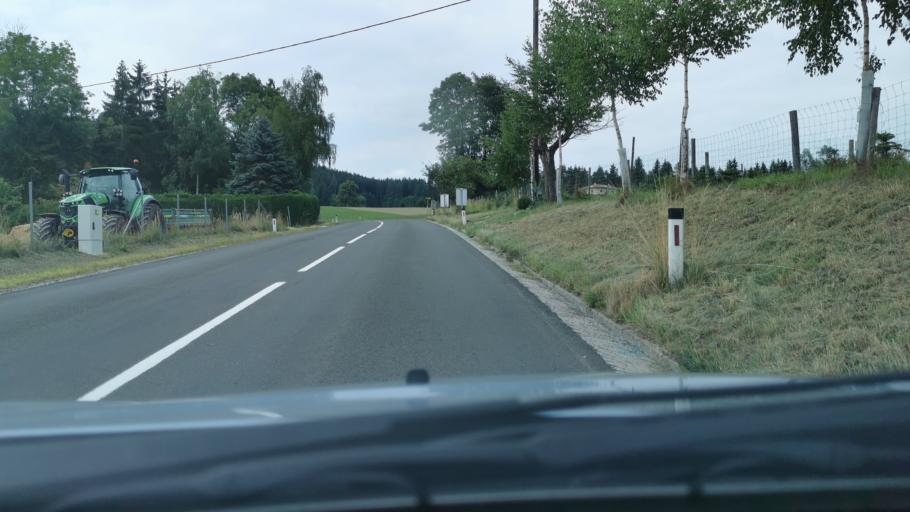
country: AT
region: Styria
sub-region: Politischer Bezirk Weiz
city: Fischbach
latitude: 47.3978
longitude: 15.6657
